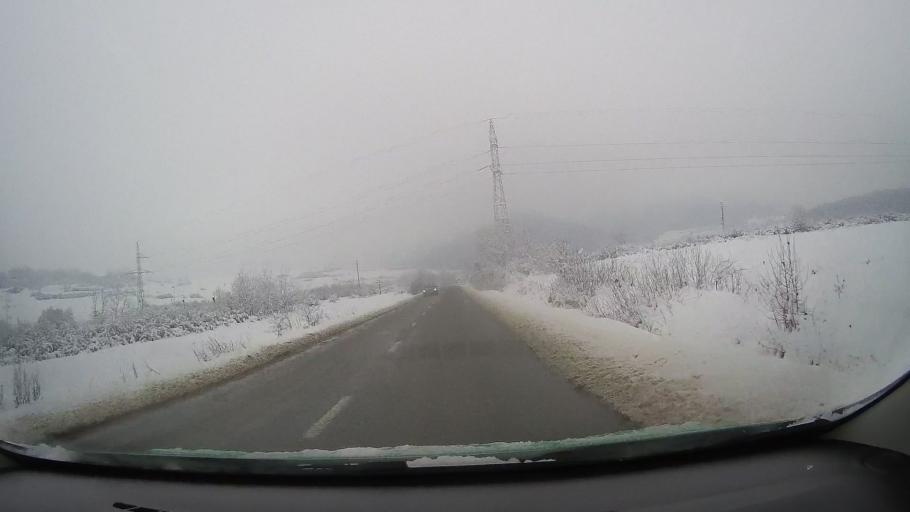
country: RO
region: Sibiu
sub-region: Comuna Orlat
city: Orlat
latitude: 45.7754
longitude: 23.9456
